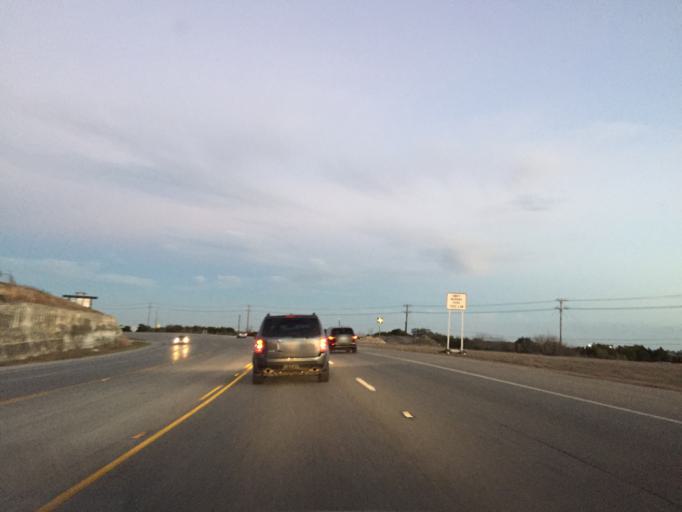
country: US
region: Texas
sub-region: Williamson County
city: Cedar Park
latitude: 30.5122
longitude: -97.8635
